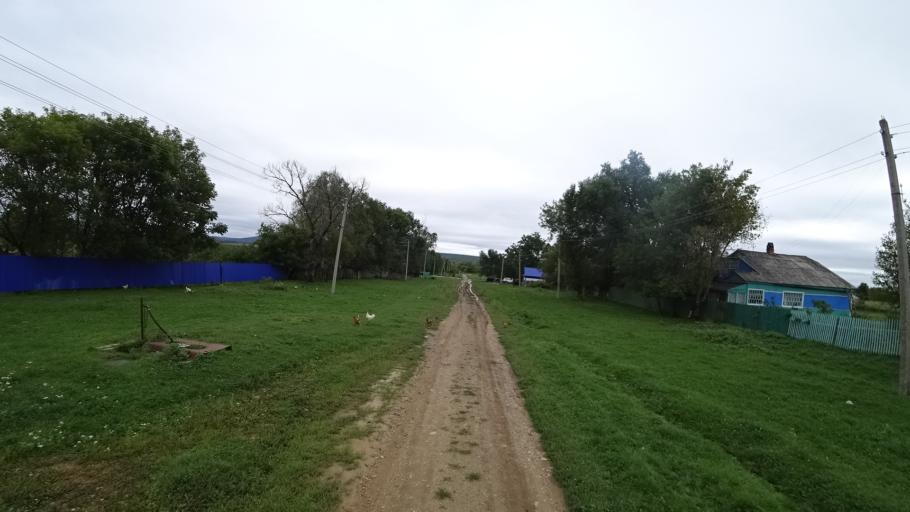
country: RU
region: Primorskiy
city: Rettikhovka
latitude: 44.1378
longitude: 132.6522
